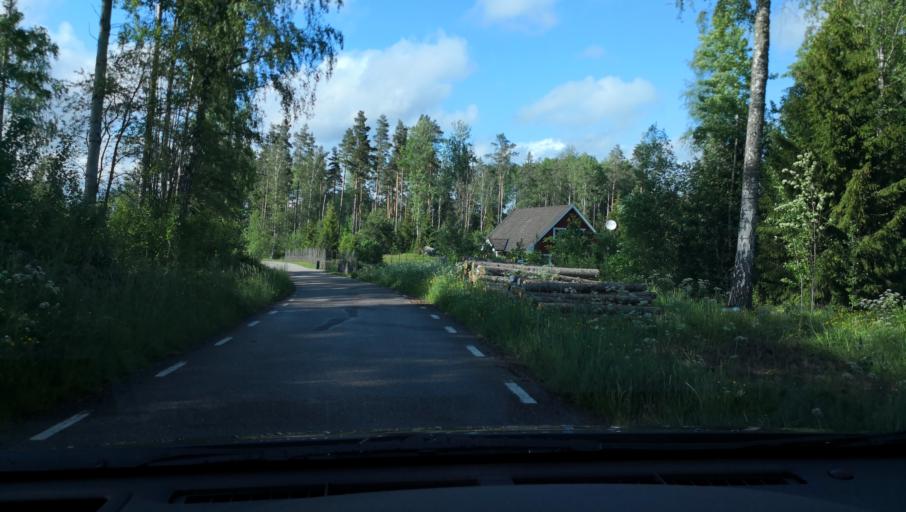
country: SE
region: OErebro
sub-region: Lindesbergs Kommun
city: Fellingsbro
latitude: 59.3318
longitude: 15.6867
